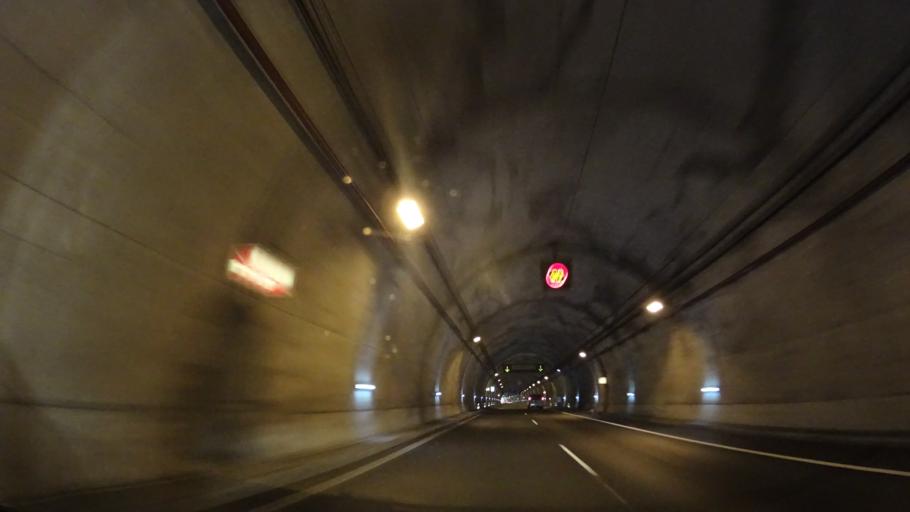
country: ES
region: Asturias
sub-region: Province of Asturias
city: Ribadesella
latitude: 43.4670
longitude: -5.1502
